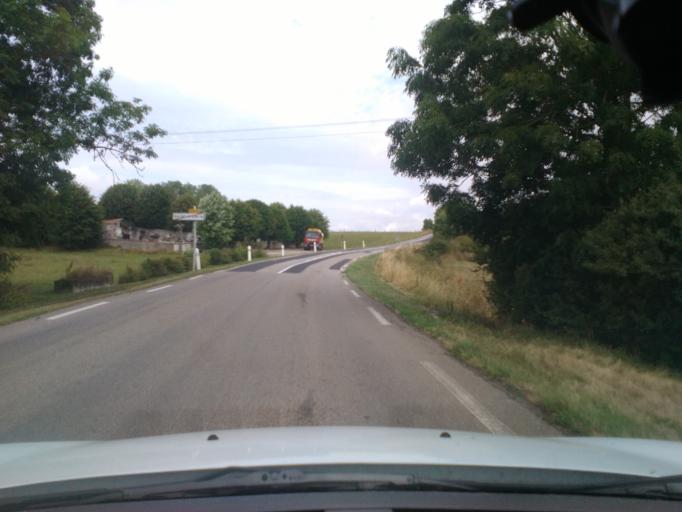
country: FR
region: Lorraine
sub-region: Departement de Meurthe-et-Moselle
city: Vezelise
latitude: 48.4237
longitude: 6.1273
